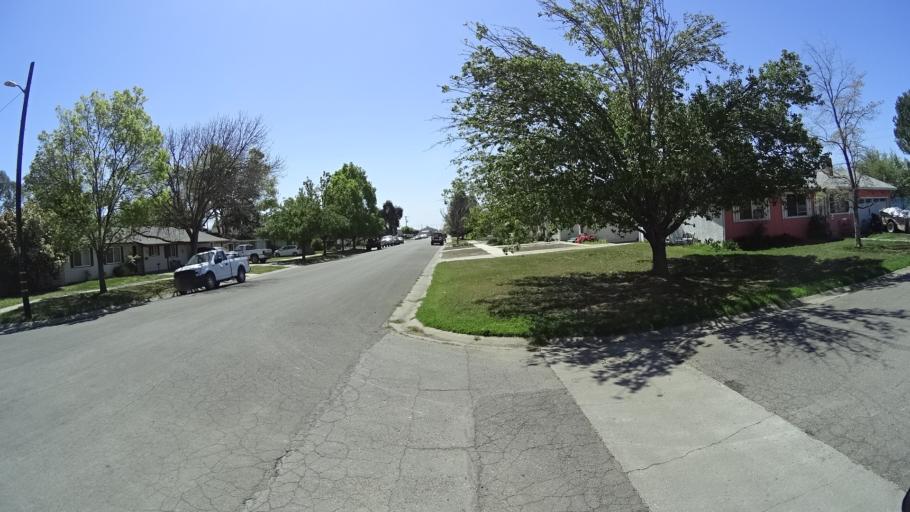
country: US
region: California
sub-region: Glenn County
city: Willows
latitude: 39.5192
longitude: -122.1909
